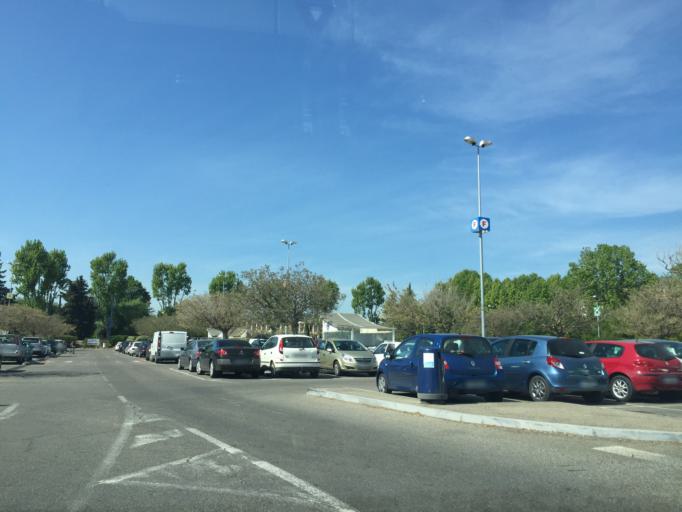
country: FR
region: Provence-Alpes-Cote d'Azur
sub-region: Departement des Alpes-de-Haute-Provence
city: Manosque
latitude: 43.8193
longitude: 5.7982
